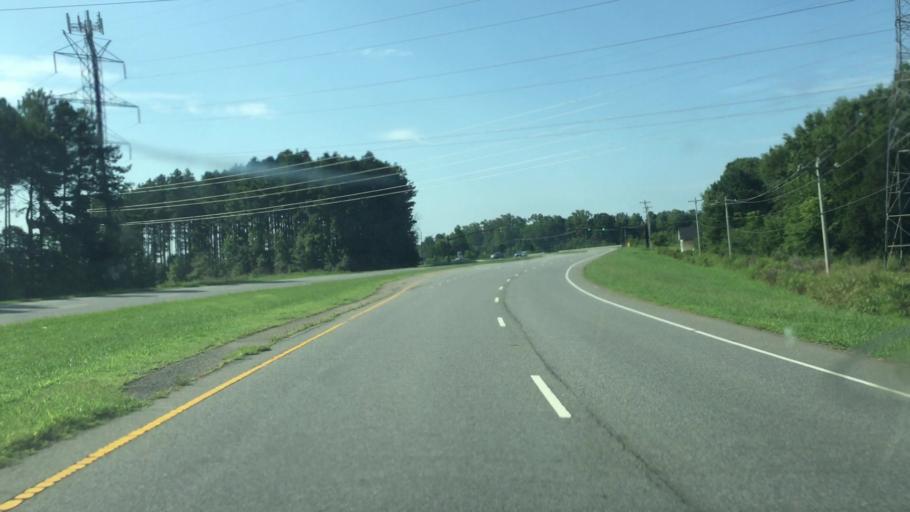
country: US
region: North Carolina
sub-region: Cabarrus County
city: Kannapolis
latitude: 35.4720
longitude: -80.6707
